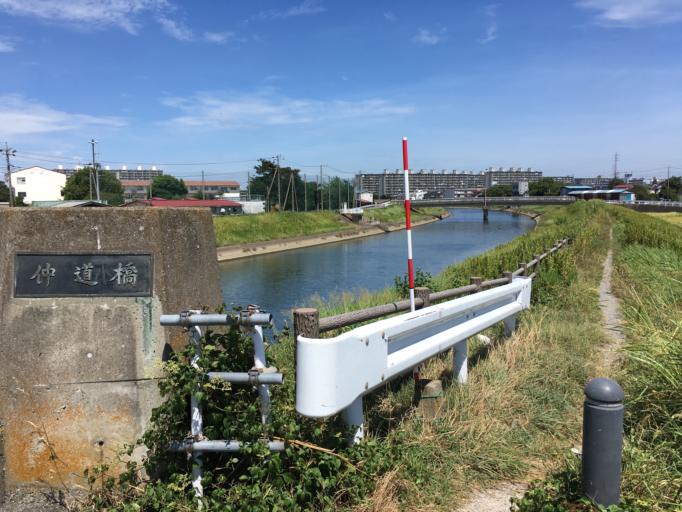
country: JP
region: Chiba
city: Nagareyama
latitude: 35.8234
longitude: 139.9023
